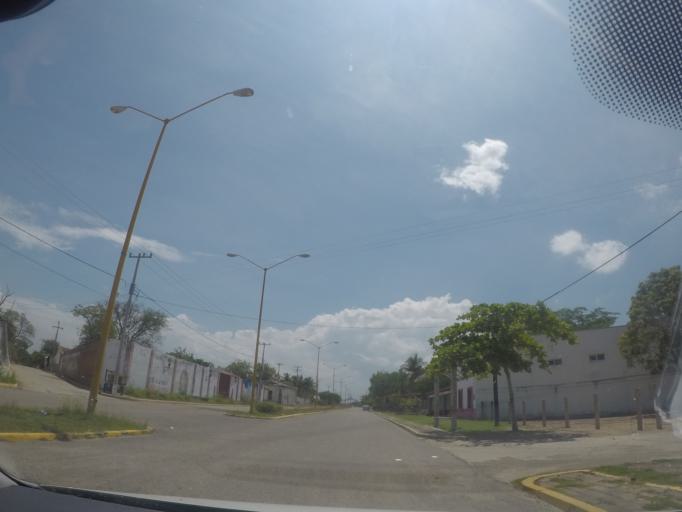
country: MX
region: Oaxaca
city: San Francisco Ixhuatan
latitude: 16.4011
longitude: -94.4556
